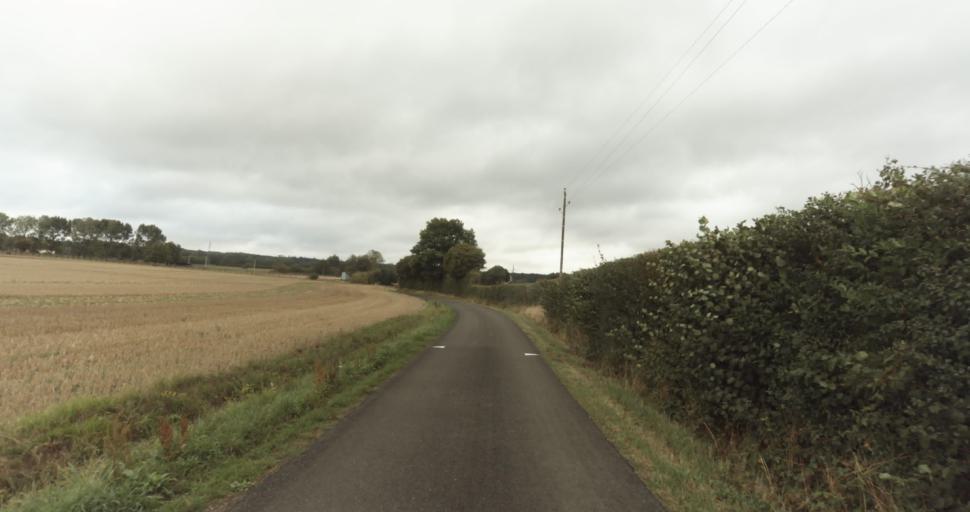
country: FR
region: Lower Normandy
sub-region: Departement de l'Orne
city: Sainte-Gauburge-Sainte-Colombe
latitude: 48.7390
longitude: 0.4707
